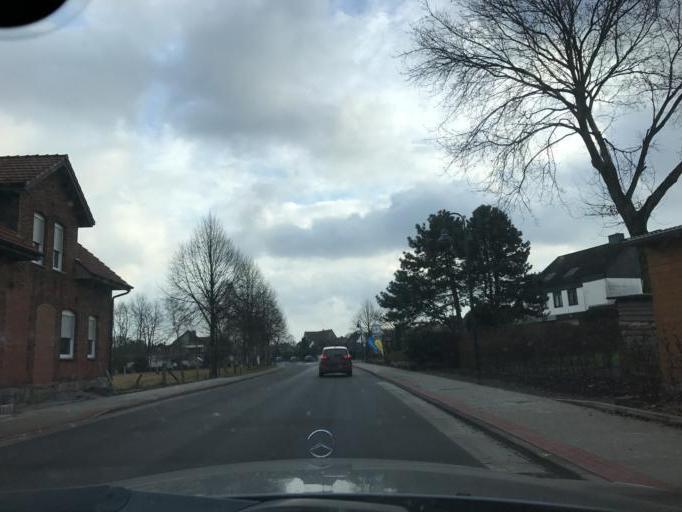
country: DE
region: Lower Saxony
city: Hasbergen
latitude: 52.2019
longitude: 7.9339
